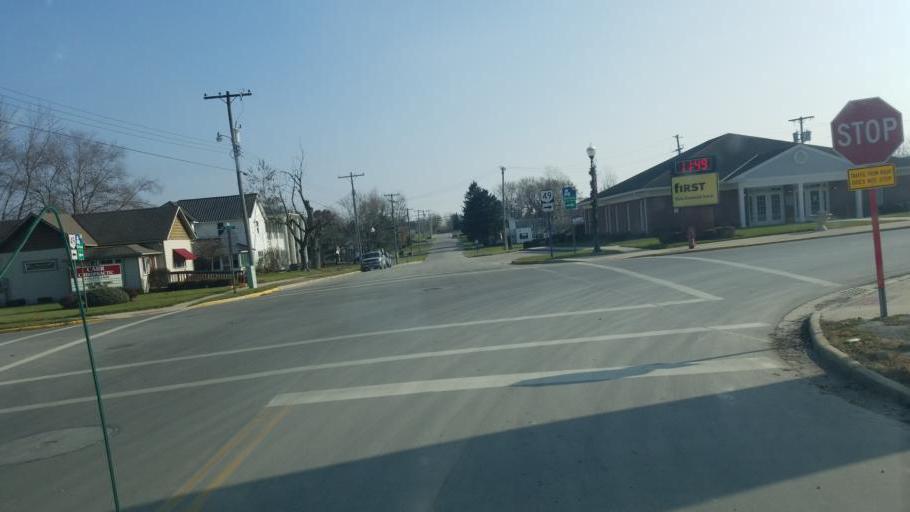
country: US
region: Ohio
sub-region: Mercer County
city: Fort Recovery
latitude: 40.4152
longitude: -84.7796
